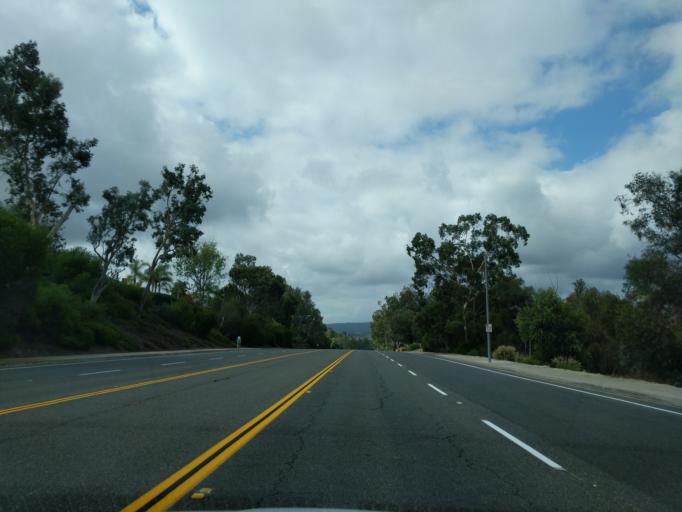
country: US
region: California
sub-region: Orange County
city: Mission Viejo
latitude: 33.5836
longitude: -117.6913
